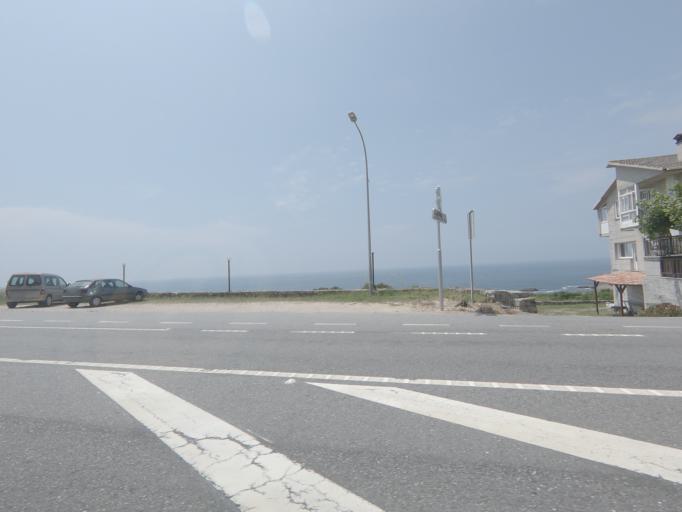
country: ES
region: Galicia
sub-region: Provincia de Pontevedra
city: A Guarda
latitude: 41.9144
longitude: -8.8793
